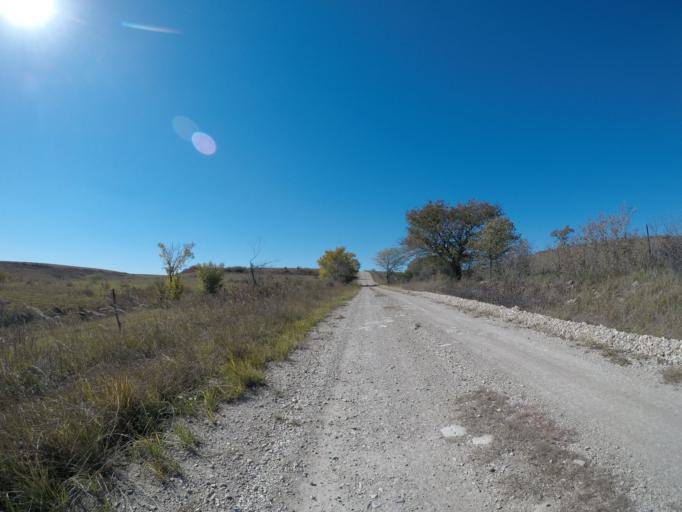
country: US
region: Kansas
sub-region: Wabaunsee County
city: Alma
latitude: 39.0290
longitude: -96.3937
